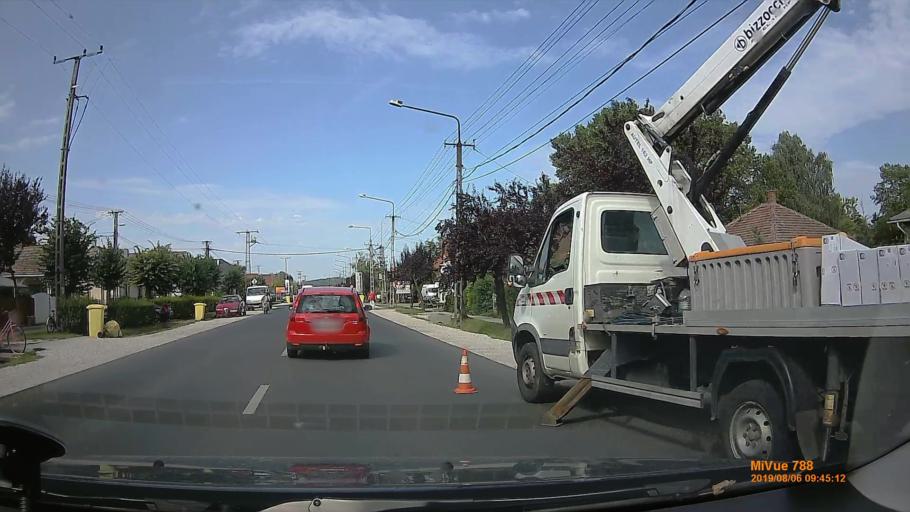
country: HU
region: Somogy
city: Balatonlelle
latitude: 46.7858
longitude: 17.6920
